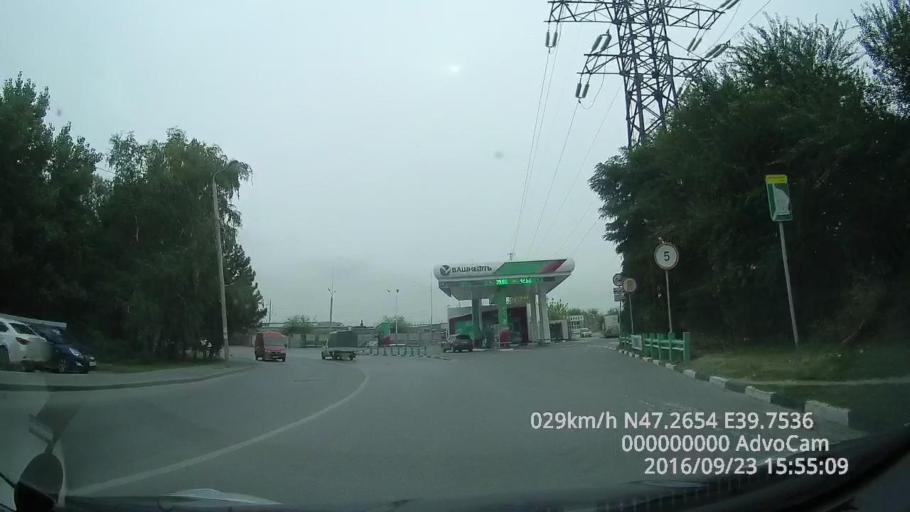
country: RU
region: Rostov
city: Imeni Chkalova
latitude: 47.2653
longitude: 39.7535
